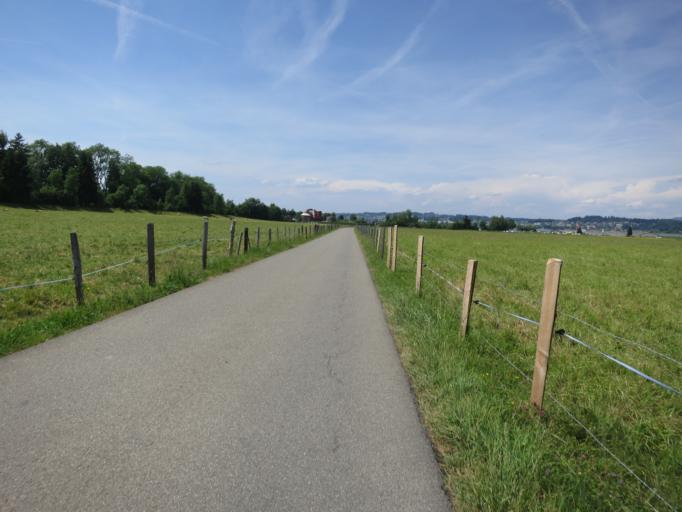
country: CH
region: Schwyz
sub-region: Bezirk March
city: Lachen
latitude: 47.1985
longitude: 8.8670
